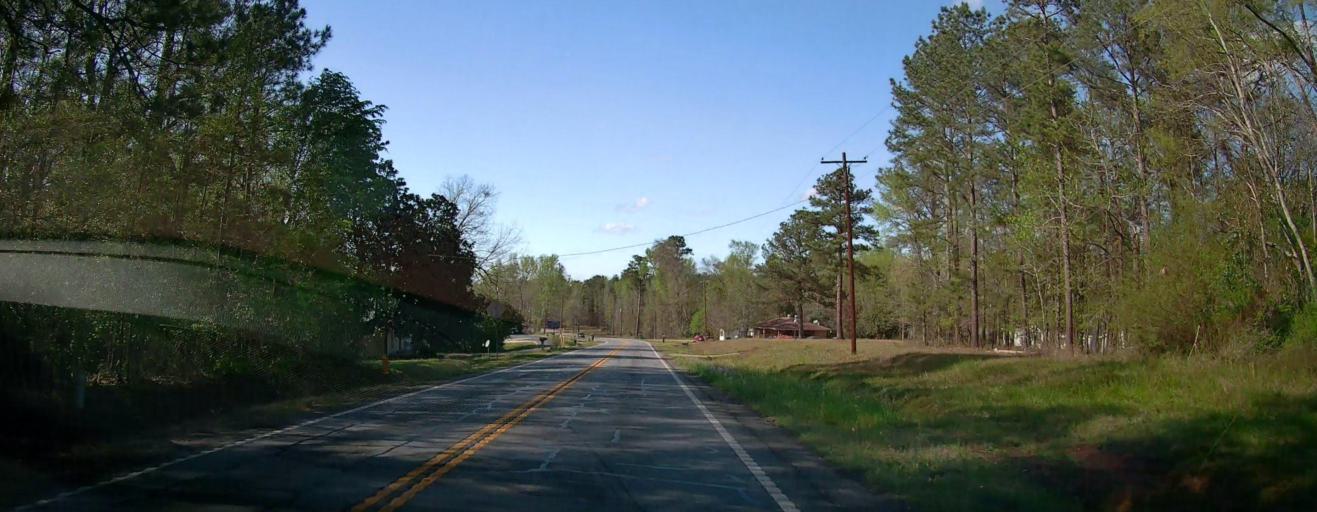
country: US
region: Georgia
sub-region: Baldwin County
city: Hardwick
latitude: 33.0849
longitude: -83.1710
